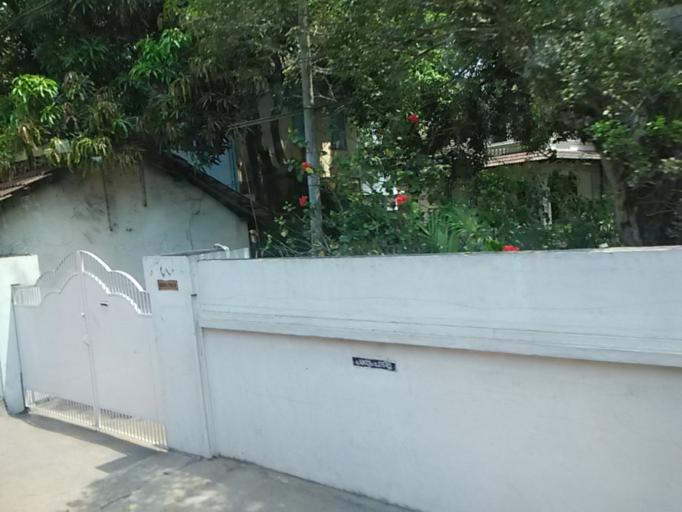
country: IN
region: Kerala
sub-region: Kozhikode
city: Kozhikode
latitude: 11.2661
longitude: 75.7770
